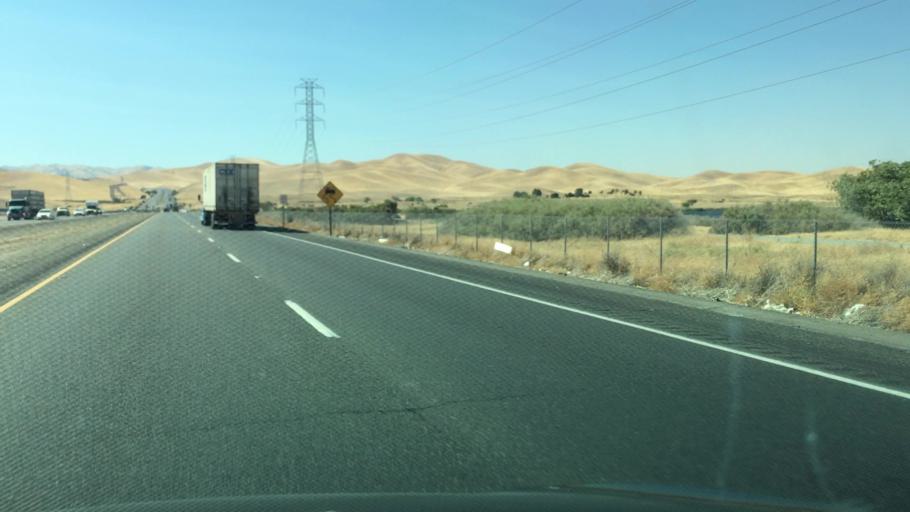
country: US
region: California
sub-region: Merced County
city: Gustine
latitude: 37.0656
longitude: -121.0648
